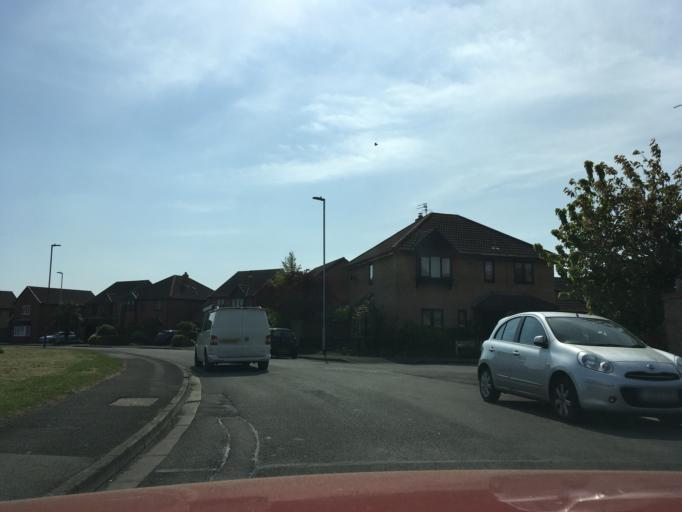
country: GB
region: England
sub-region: South Gloucestershire
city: Almondsbury
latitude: 51.5442
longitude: -2.5504
